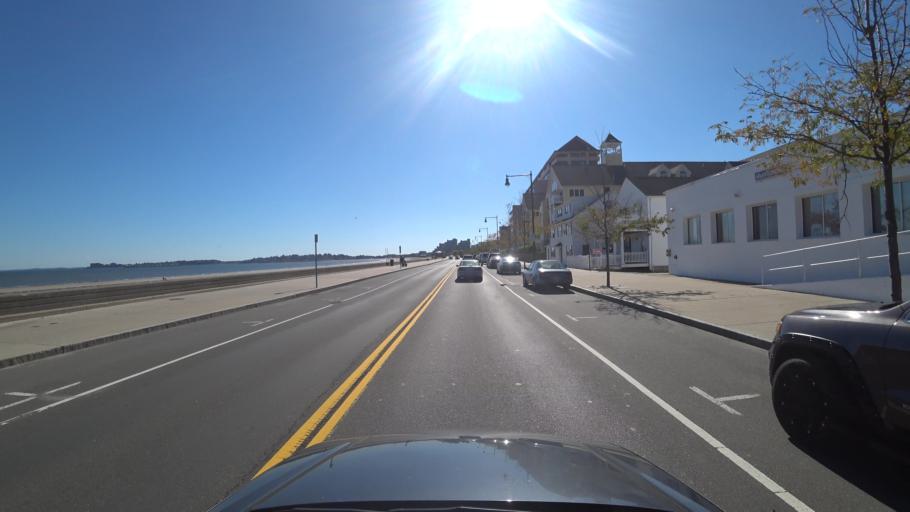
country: US
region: Massachusetts
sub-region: Suffolk County
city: Revere
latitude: 42.4219
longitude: -70.9849
